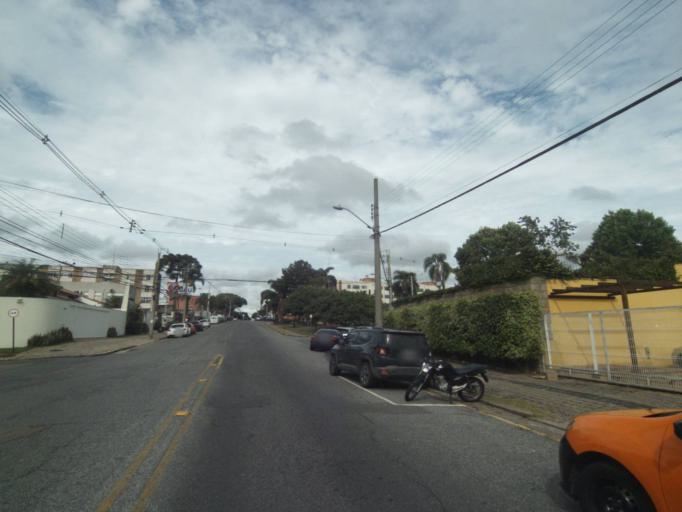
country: BR
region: Parana
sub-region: Curitiba
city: Curitiba
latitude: -25.4431
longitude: -49.3009
